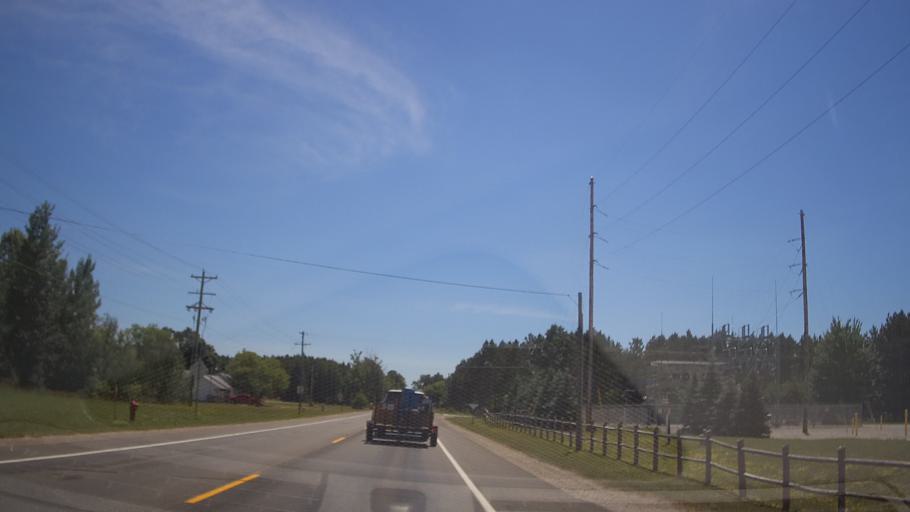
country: US
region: Michigan
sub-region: Grand Traverse County
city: Traverse City
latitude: 44.6554
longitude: -85.6965
